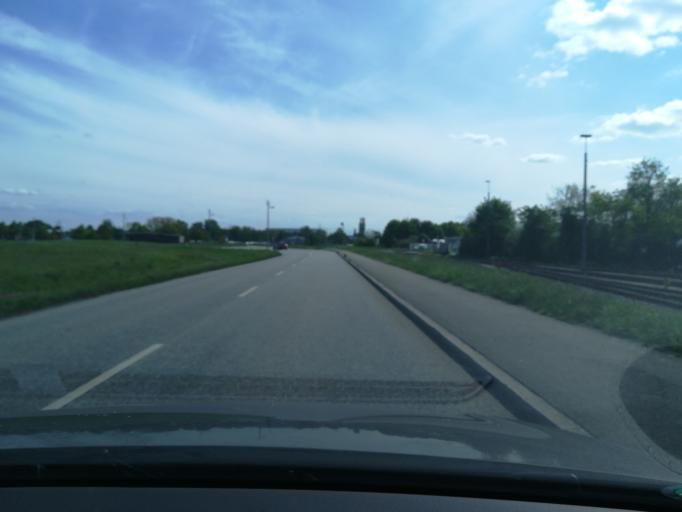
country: DE
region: Hamburg
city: Harburg
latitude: 53.4838
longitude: 9.9875
